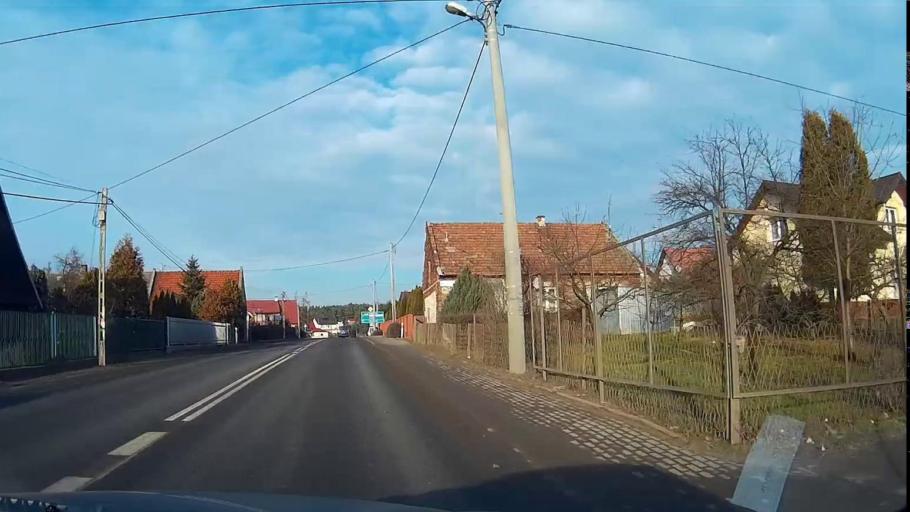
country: PL
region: Lesser Poland Voivodeship
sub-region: Powiat krakowski
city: Kryspinow
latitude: 50.0448
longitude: 19.7983
